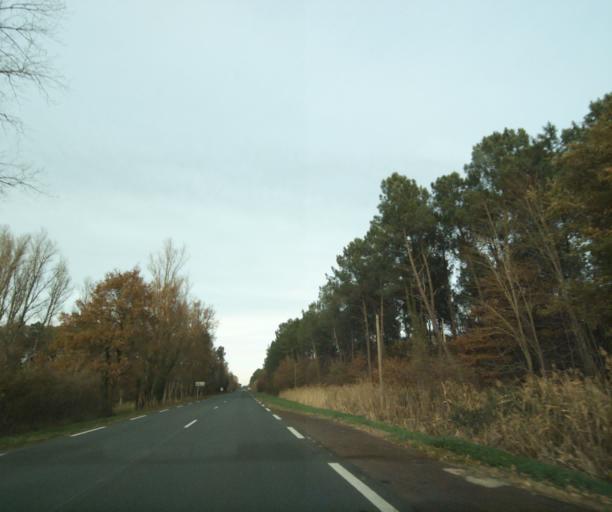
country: FR
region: Aquitaine
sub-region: Departement de la Gironde
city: Bazas
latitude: 44.3034
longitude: -0.2546
